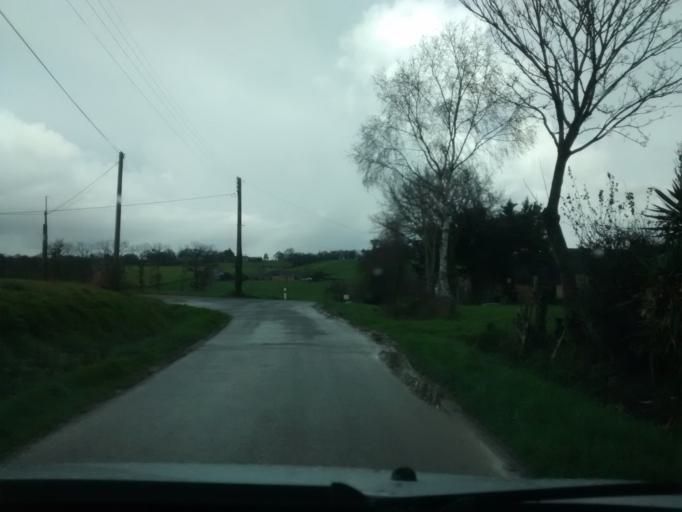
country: FR
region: Brittany
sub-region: Departement d'Ille-et-Vilaine
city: Liffre
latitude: 48.1907
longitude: -1.4963
